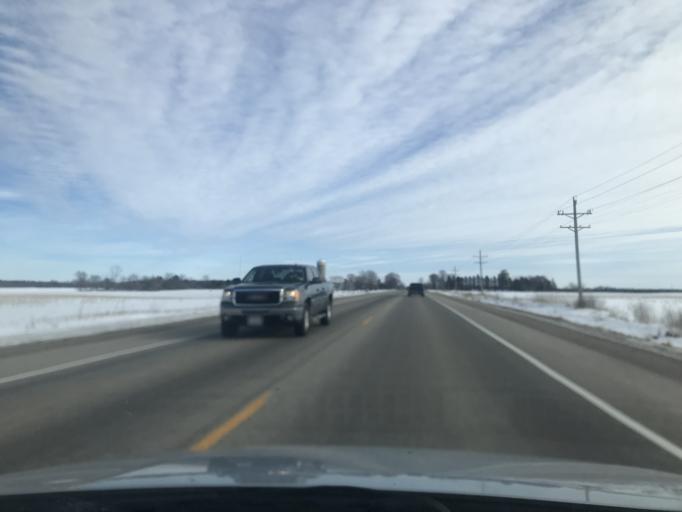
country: US
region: Wisconsin
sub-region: Oconto County
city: Gillett
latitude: 44.8963
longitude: -88.2737
